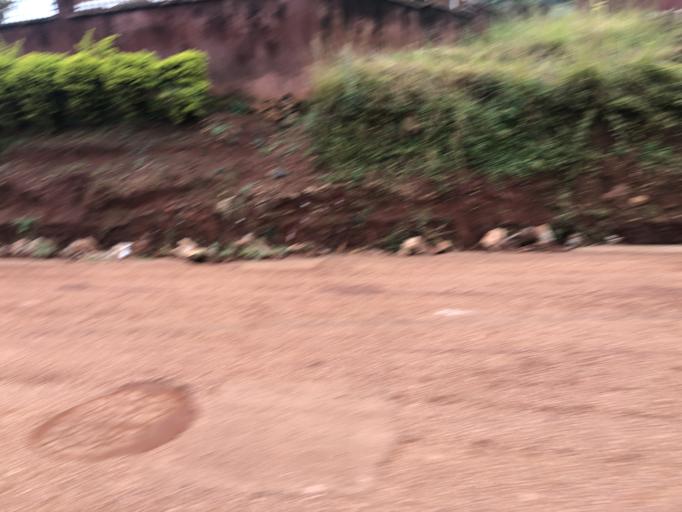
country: UG
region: Central Region
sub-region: Kampala District
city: Kampala
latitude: 0.2787
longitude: 32.6001
